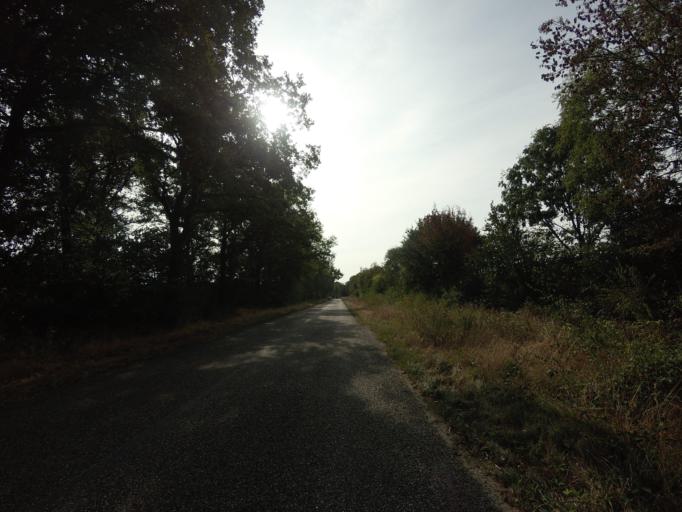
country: NL
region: North Brabant
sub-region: Gemeente Mill en Sint Hubert
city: Wilbertoord
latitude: 51.6470
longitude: 5.7978
